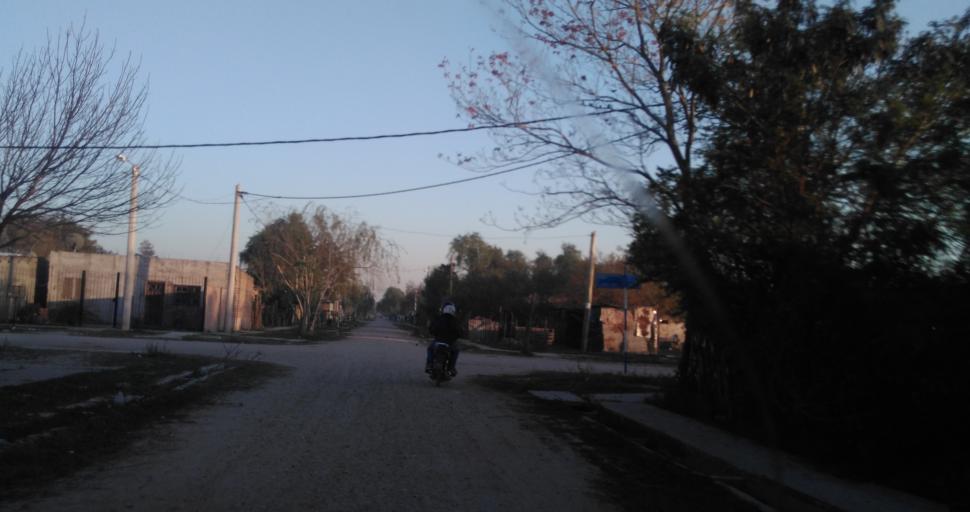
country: AR
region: Chaco
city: Resistencia
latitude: -27.4793
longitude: -59.0105
